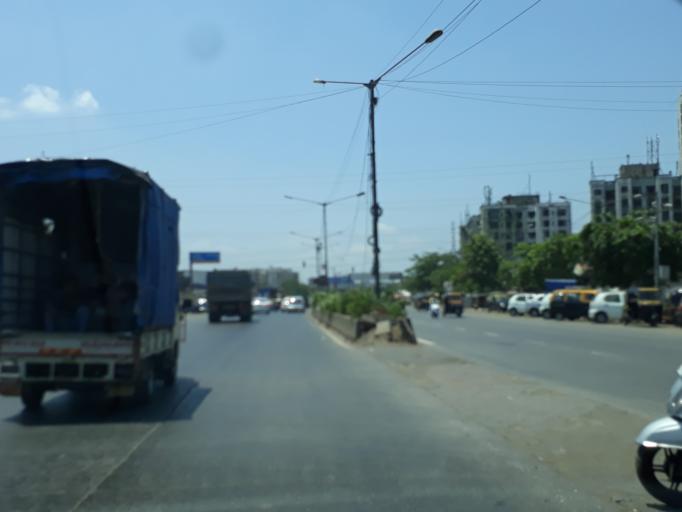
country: IN
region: Maharashtra
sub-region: Mumbai Suburban
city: Mumbai
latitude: 19.0543
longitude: 72.9346
